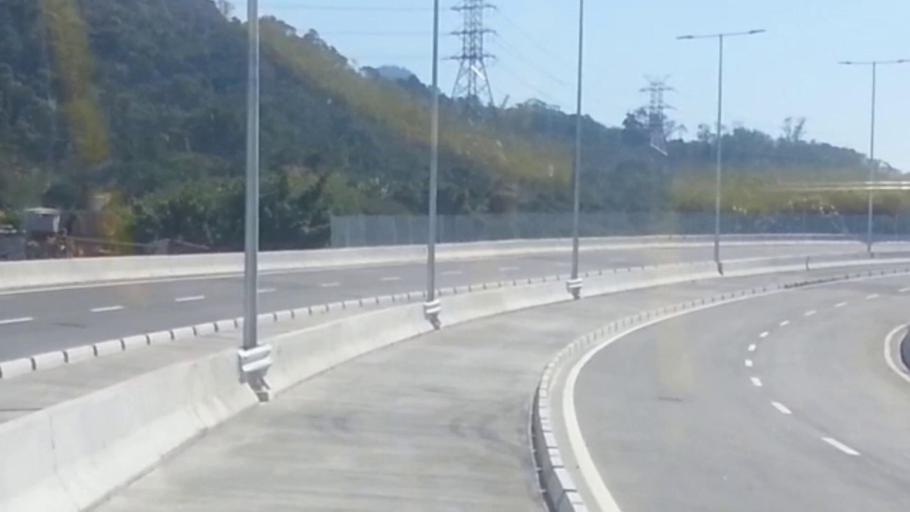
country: BR
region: Rio de Janeiro
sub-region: Nilopolis
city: Nilopolis
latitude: -22.9584
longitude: -43.3933
